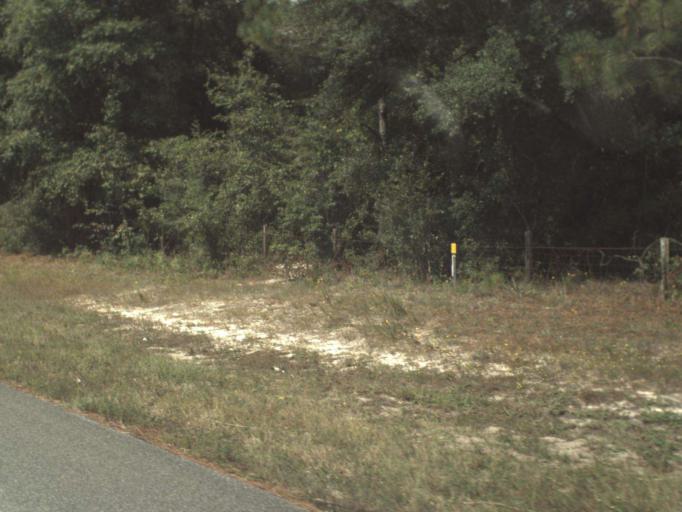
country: US
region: Florida
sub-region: Walton County
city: Freeport
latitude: 30.4773
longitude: -86.0448
